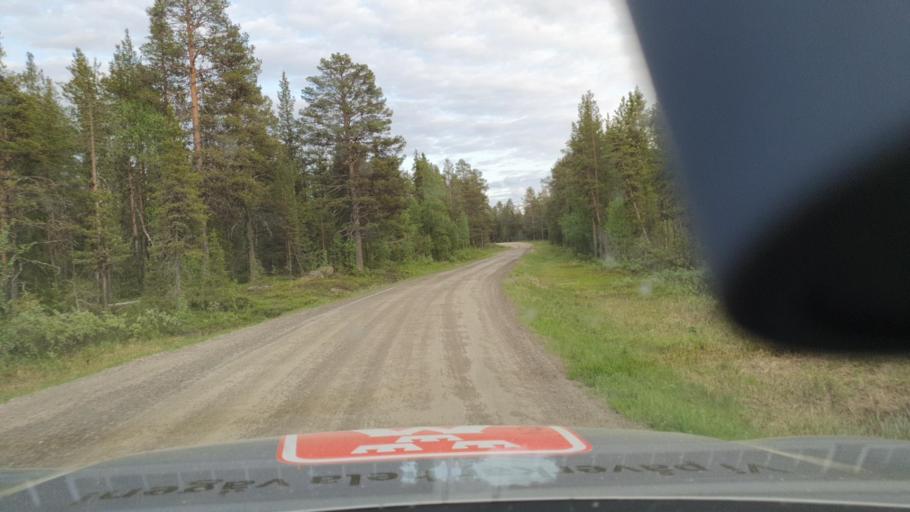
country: SE
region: Norrbotten
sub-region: Gallivare Kommun
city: Gaellivare
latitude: 66.6764
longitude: 21.2005
